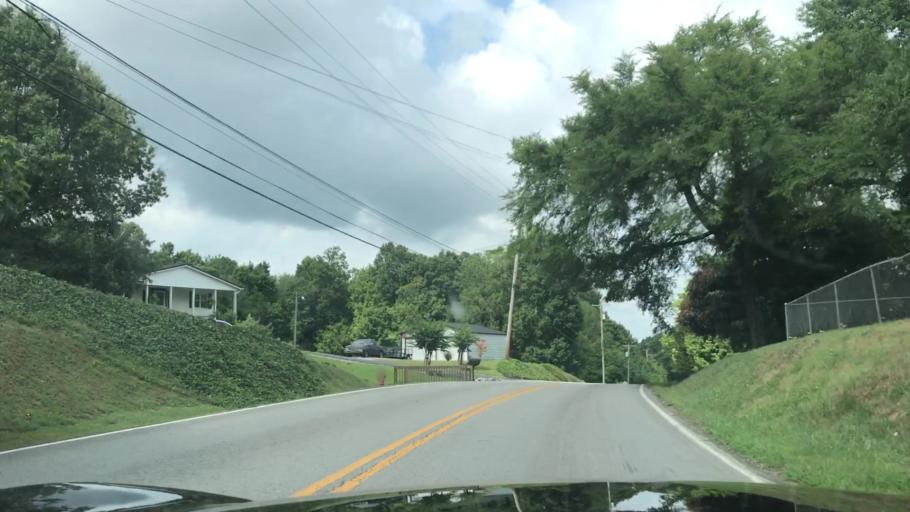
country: US
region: Kentucky
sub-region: Muhlenberg County
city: Central City
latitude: 37.2137
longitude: -87.0584
